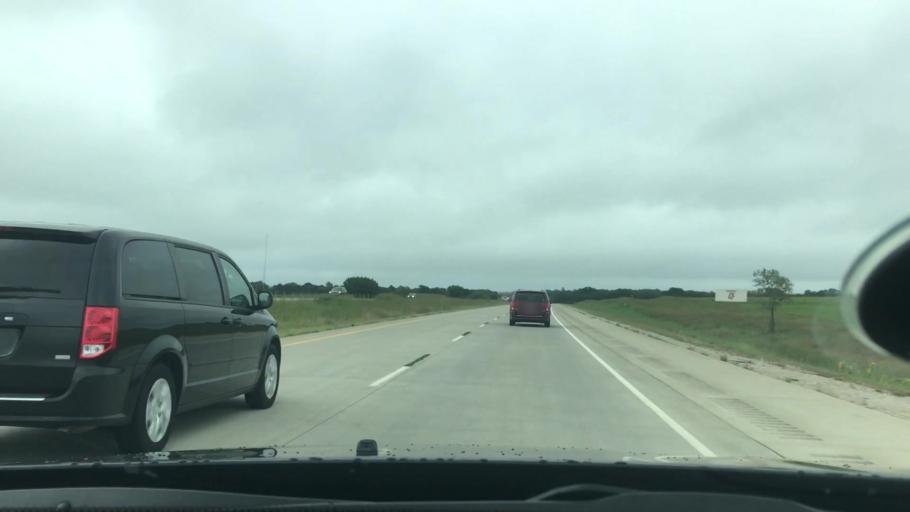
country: US
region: Oklahoma
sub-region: Okfuskee County
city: Boley
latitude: 35.3853
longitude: -96.4930
